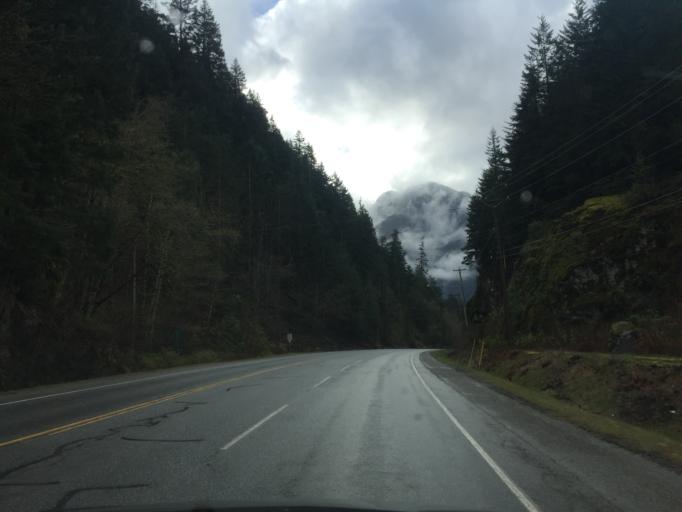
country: CA
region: British Columbia
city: Hope
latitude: 49.3672
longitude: -121.4488
